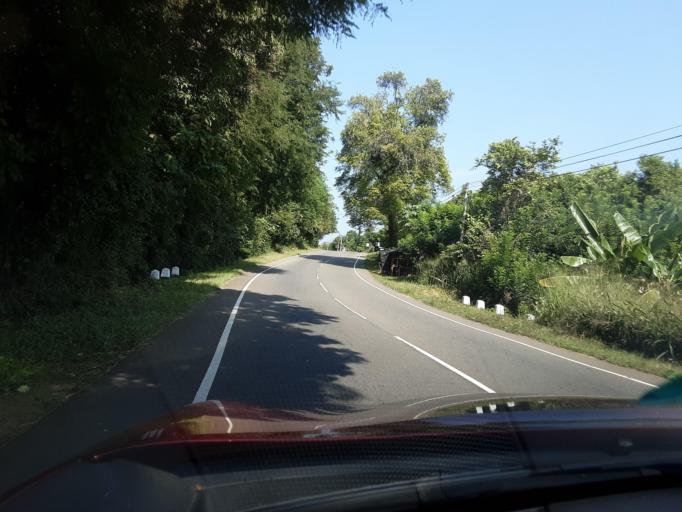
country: LK
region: Uva
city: Badulla
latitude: 7.1754
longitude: 81.0496
